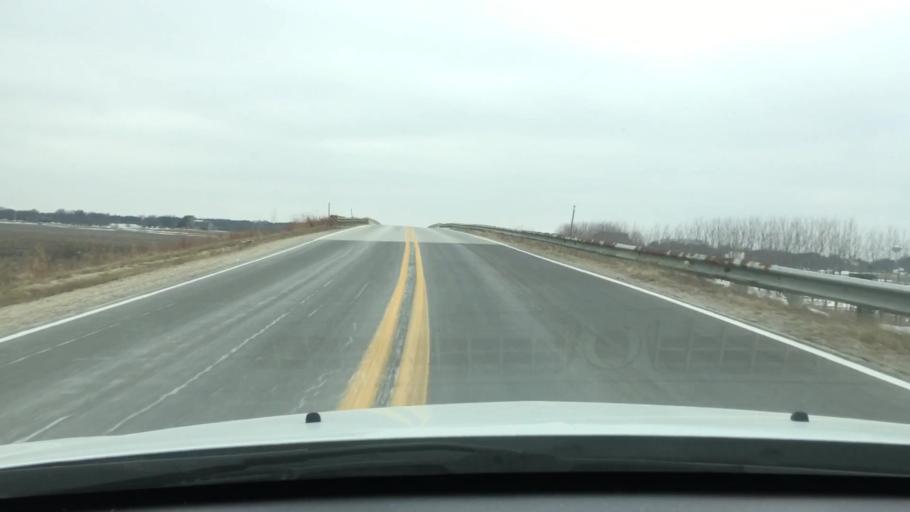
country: US
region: Illinois
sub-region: DeKalb County
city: Waterman
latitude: 41.7693
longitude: -88.8547
